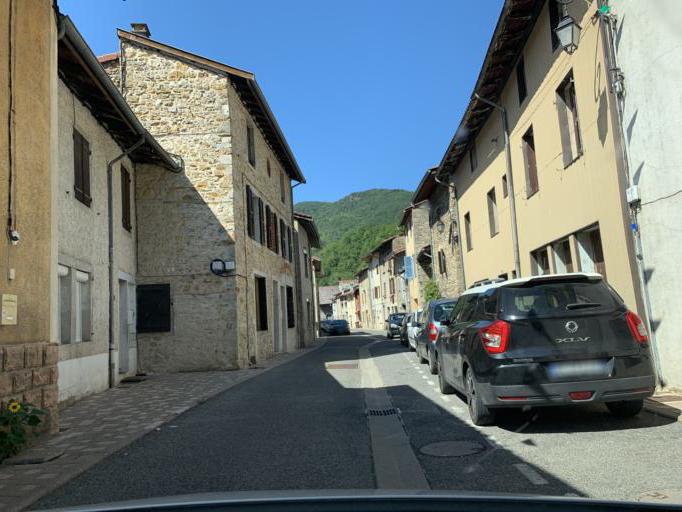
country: FR
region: Rhone-Alpes
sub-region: Departement de l'Ain
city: Vaux-en-Bugey
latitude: 45.9216
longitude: 5.3966
